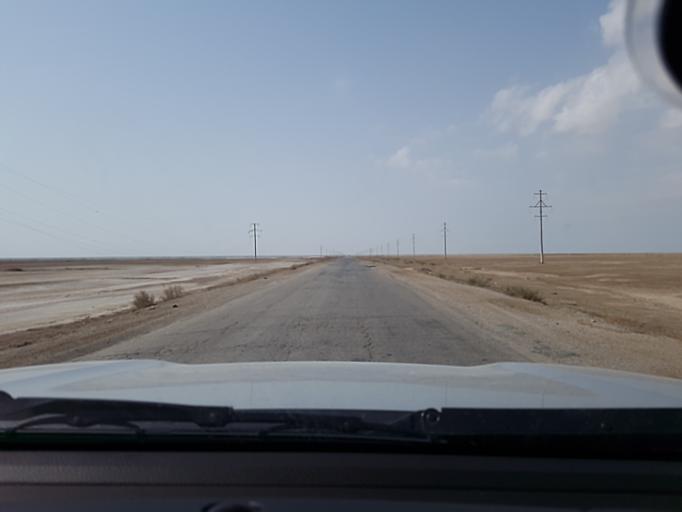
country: TM
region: Balkan
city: Gumdag
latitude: 39.0943
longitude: 54.5841
